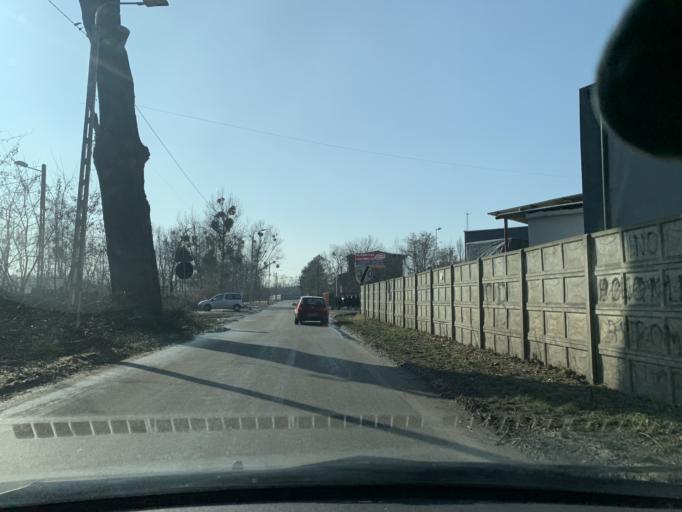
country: PL
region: Silesian Voivodeship
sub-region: Piekary Slaskie
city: Piekary Slaskie
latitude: 50.3758
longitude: 18.9137
